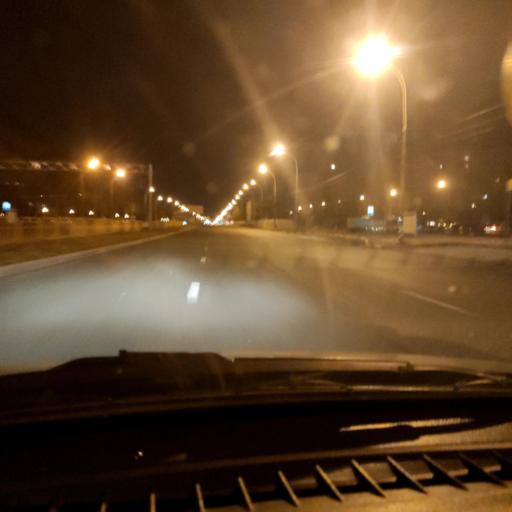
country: RU
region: Samara
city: Tol'yatti
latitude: 53.5296
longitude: 49.2819
